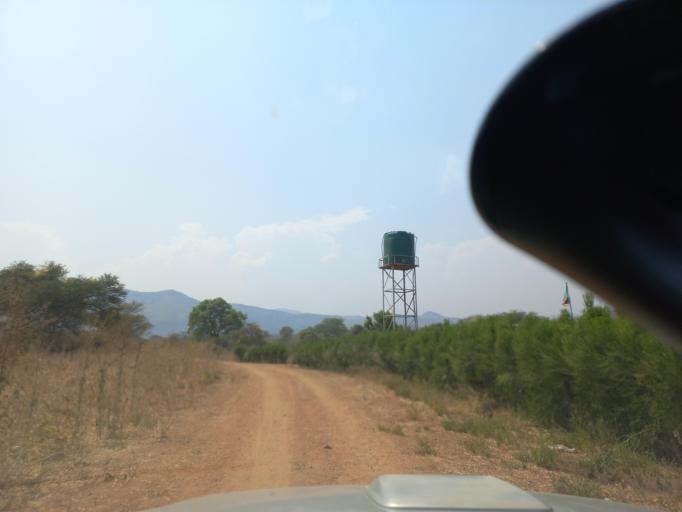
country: ZW
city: Chirundu
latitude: -15.9105
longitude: 28.6870
